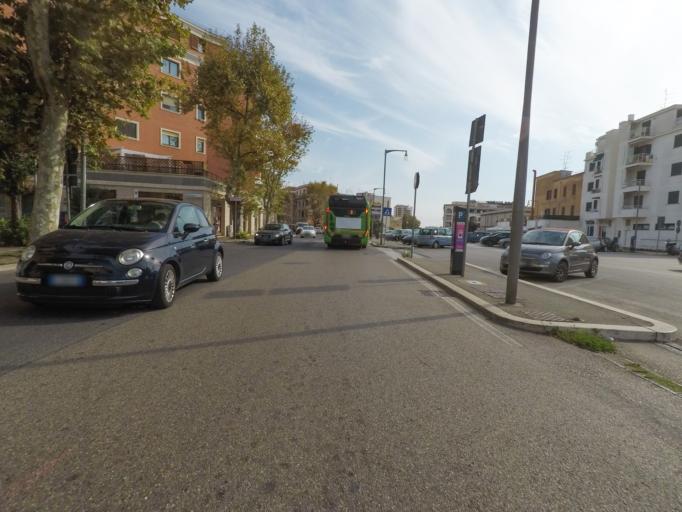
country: IT
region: Latium
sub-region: Citta metropolitana di Roma Capitale
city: Civitavecchia
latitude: 42.0948
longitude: 11.7950
